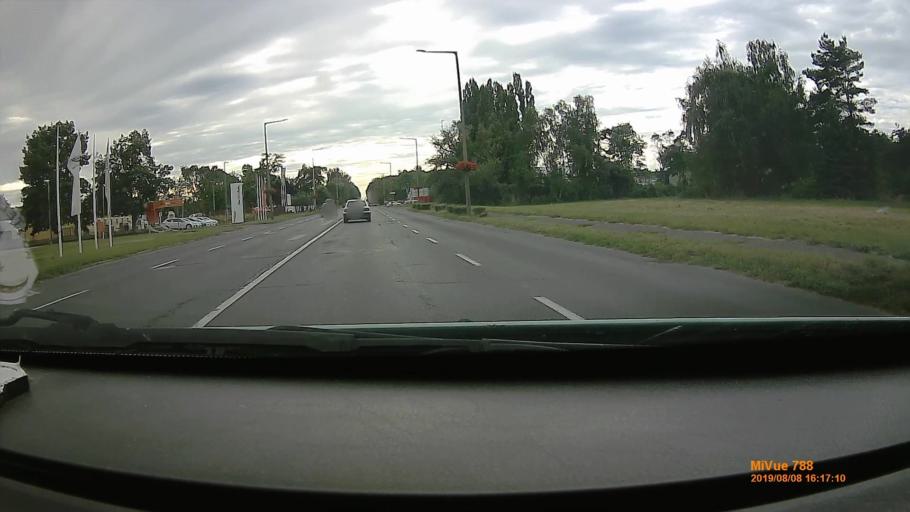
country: HU
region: Szabolcs-Szatmar-Bereg
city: Mateszalka
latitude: 47.9627
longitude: 22.2971
